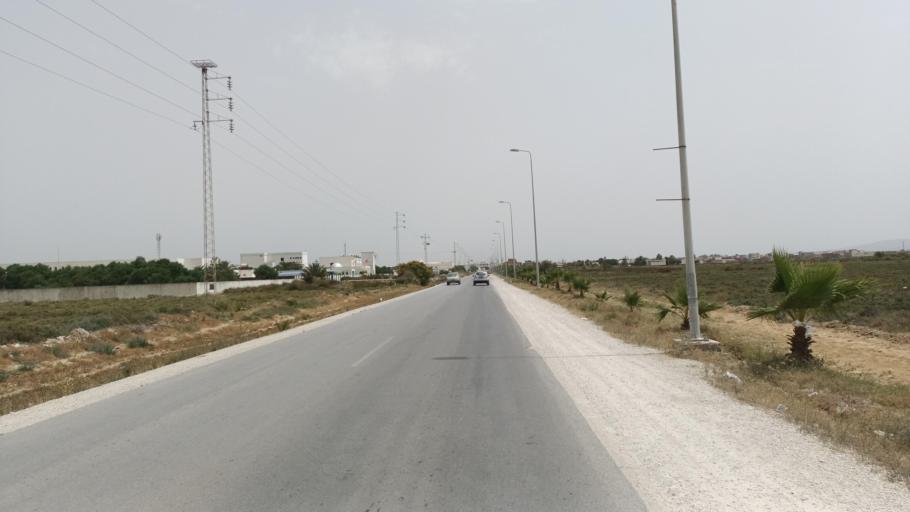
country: TN
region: Nabul
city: Manzil Bu Zalafah
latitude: 36.7142
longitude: 10.4796
